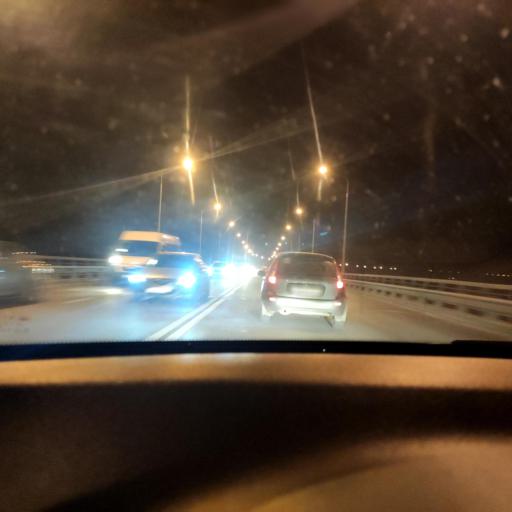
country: RU
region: Samara
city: Samara
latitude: 53.1693
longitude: 50.1956
